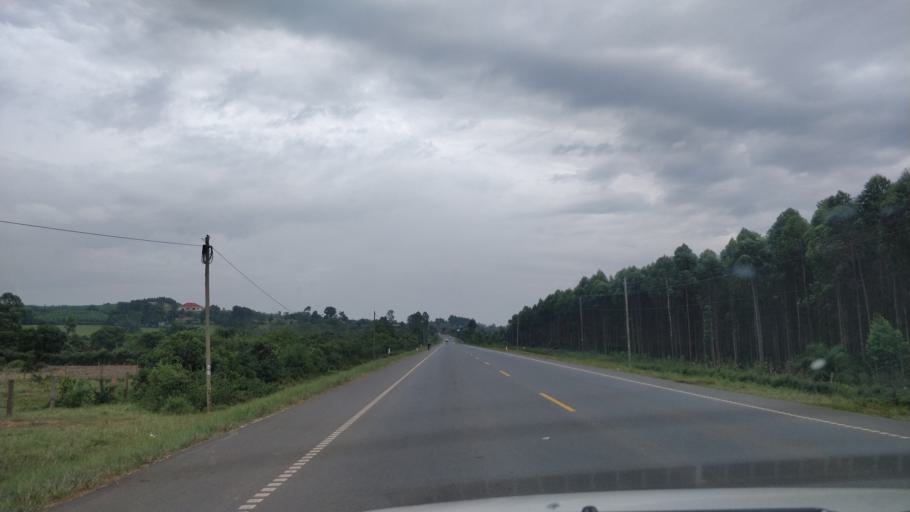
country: UG
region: Western Region
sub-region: Sheema District
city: Kibingo
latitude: -0.6570
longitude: 30.4740
